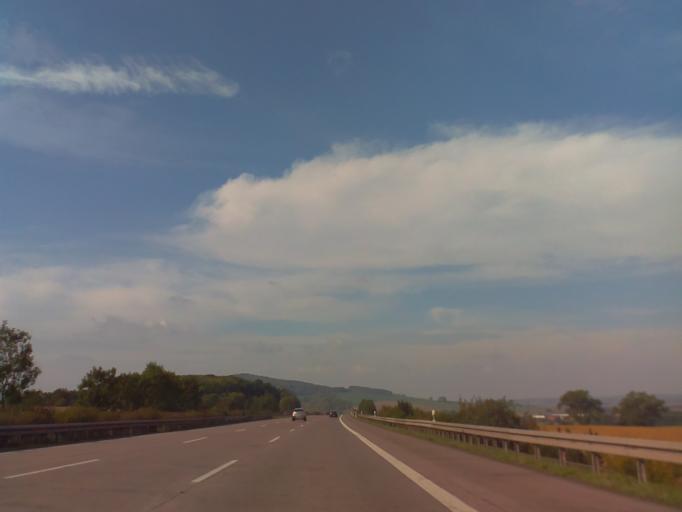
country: DE
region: Thuringia
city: Mechterstadt
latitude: 50.9296
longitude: 10.5080
